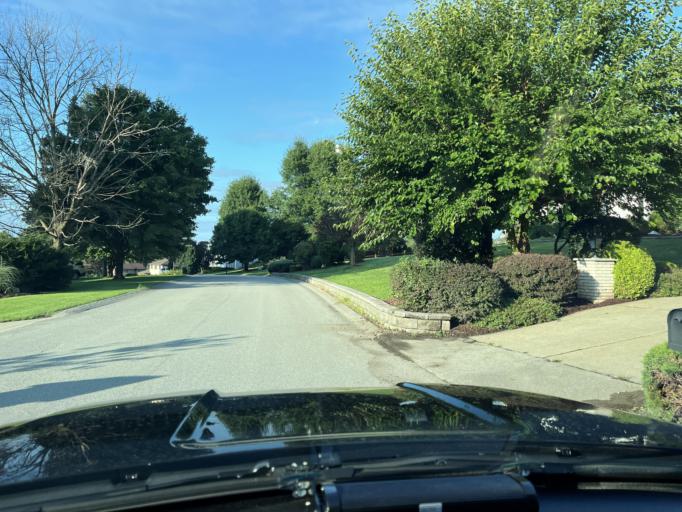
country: US
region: Pennsylvania
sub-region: Fayette County
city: Leith-Hatfield
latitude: 39.8760
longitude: -79.7261
